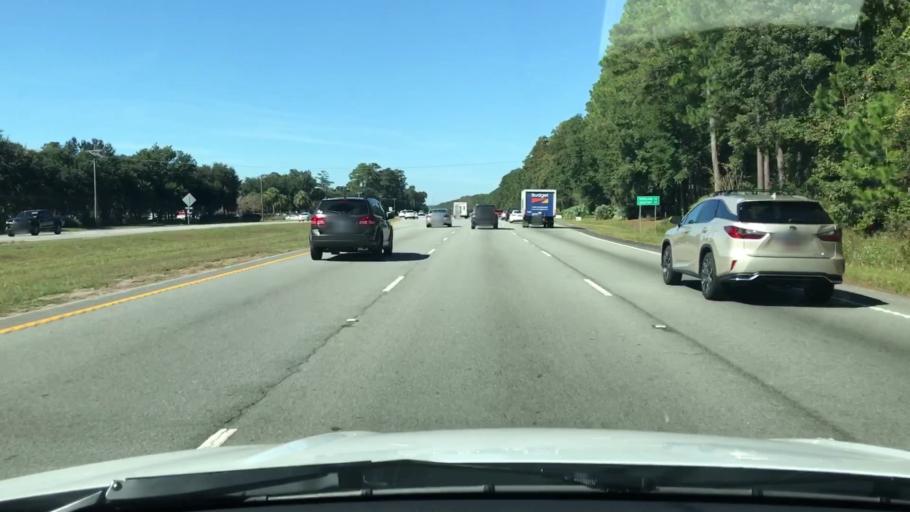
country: US
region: South Carolina
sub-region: Beaufort County
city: Bluffton
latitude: 32.2629
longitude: -80.8552
